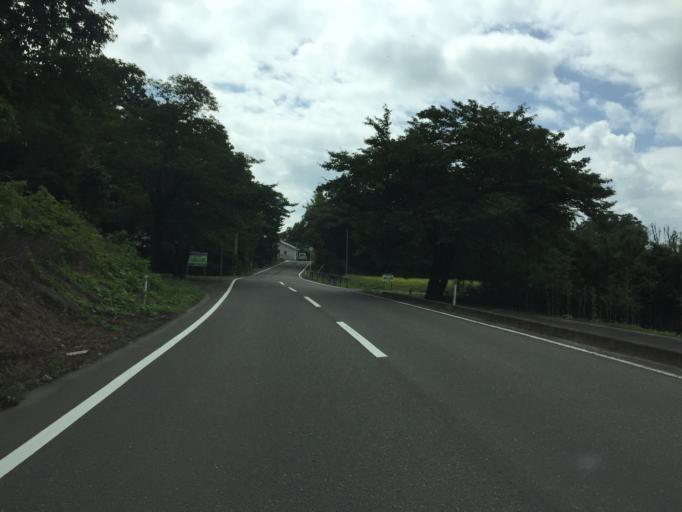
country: JP
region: Fukushima
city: Motomiya
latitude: 37.4767
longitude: 140.3375
